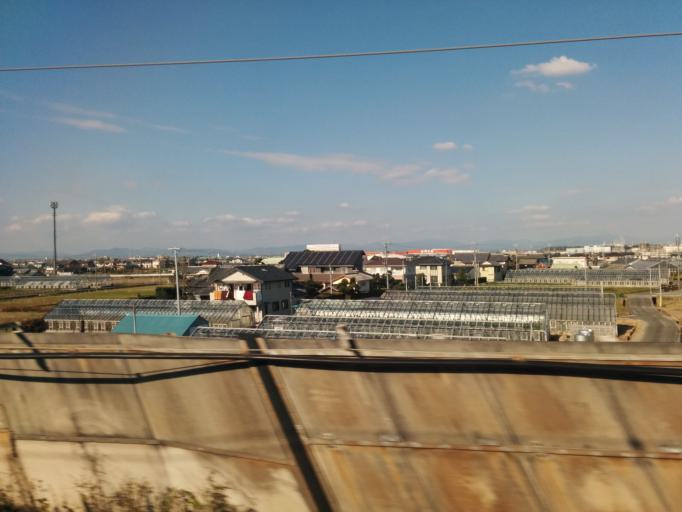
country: JP
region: Shizuoka
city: Iwata
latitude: 34.7033
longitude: 137.8351
